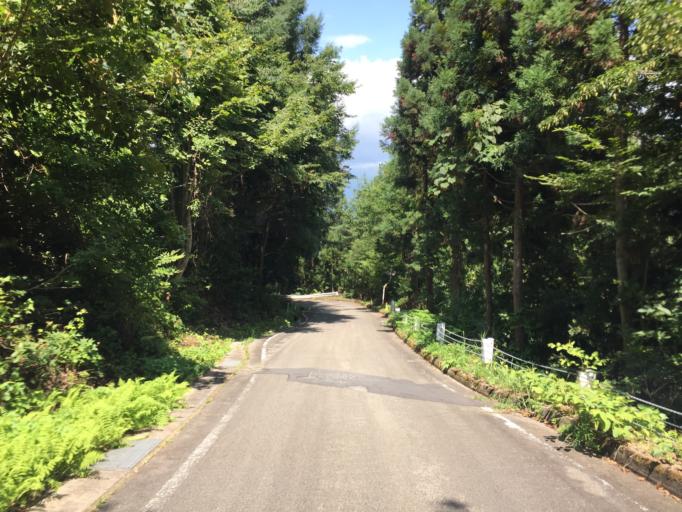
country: JP
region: Fukushima
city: Inawashiro
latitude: 37.4745
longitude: 140.0422
